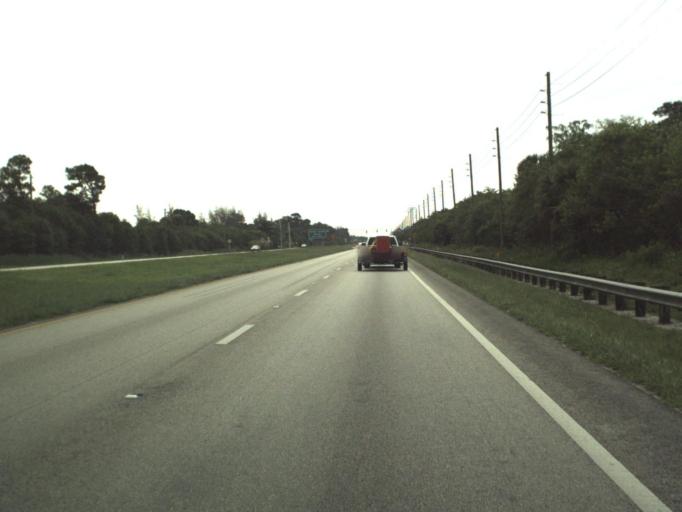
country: US
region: Florida
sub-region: Palm Beach County
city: Loxahatchee Groves
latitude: 26.6830
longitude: -80.2953
